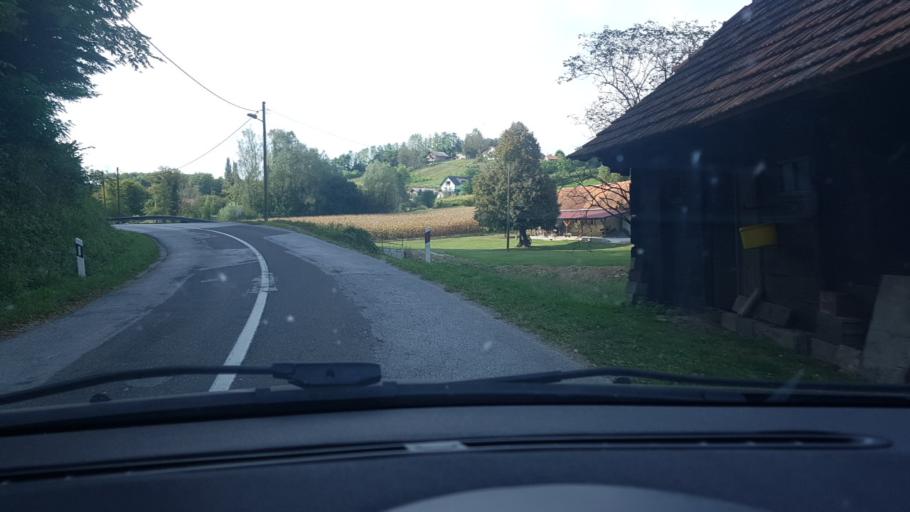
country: HR
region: Krapinsko-Zagorska
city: Mihovljan
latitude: 46.1173
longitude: 16.0059
